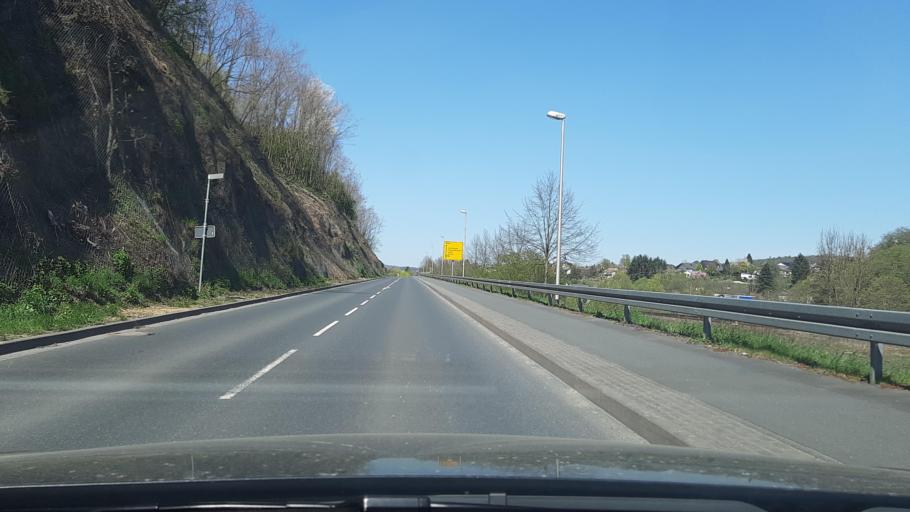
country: DE
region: Hesse
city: Weilburg
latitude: 50.4924
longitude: 8.2701
